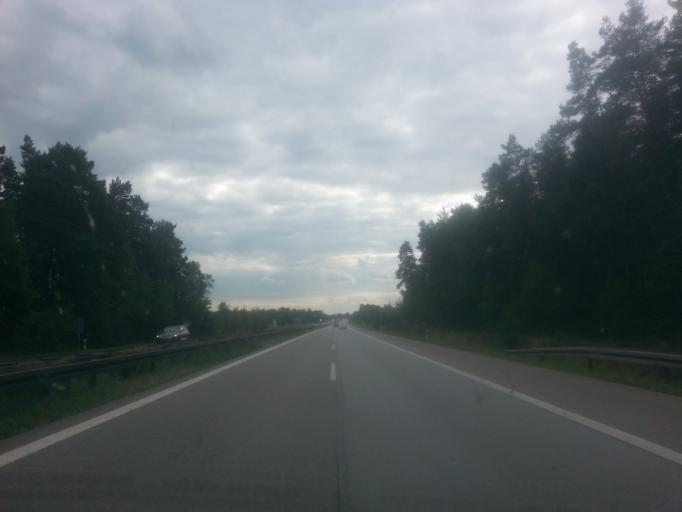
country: DE
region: Bavaria
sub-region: Upper Palatinate
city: Steinberg
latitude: 49.2835
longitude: 12.1378
